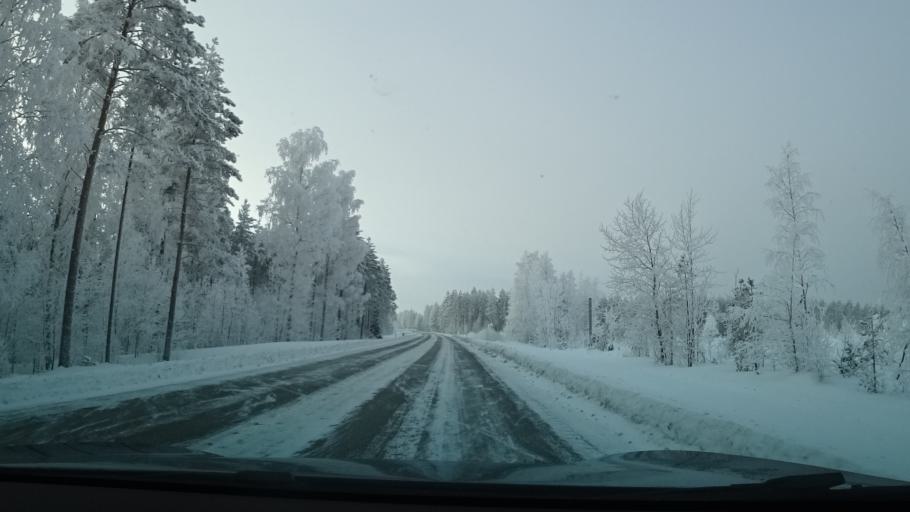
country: FI
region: South Karelia
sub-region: Imatra
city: Saari
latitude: 61.7784
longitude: 29.6996
